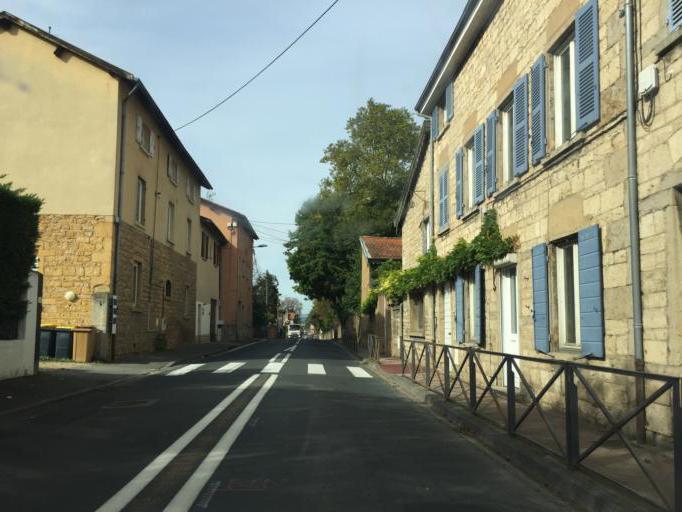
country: FR
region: Rhone-Alpes
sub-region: Departement du Rhone
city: Chasselay
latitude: 45.8727
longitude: 4.7703
